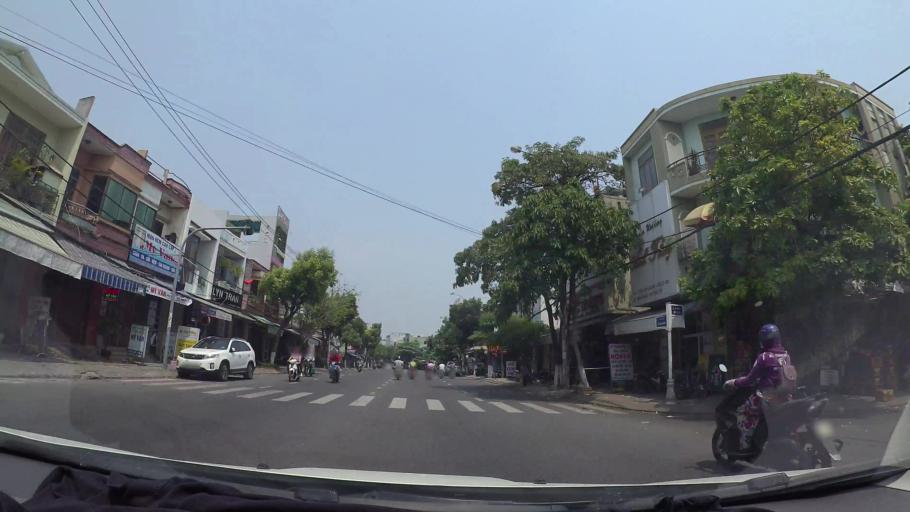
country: VN
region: Da Nang
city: Cam Le
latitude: 16.0128
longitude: 108.2057
